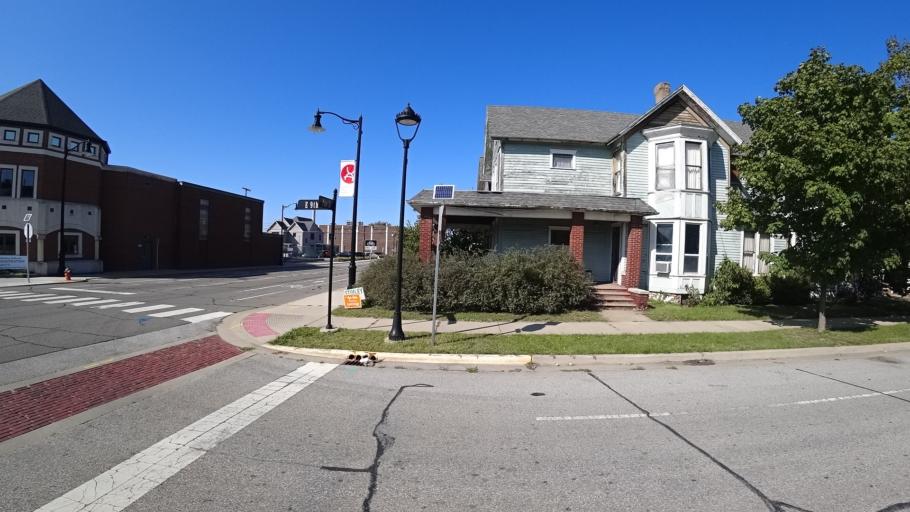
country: US
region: Indiana
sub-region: LaPorte County
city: Michigan City
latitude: 41.7133
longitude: -86.8980
